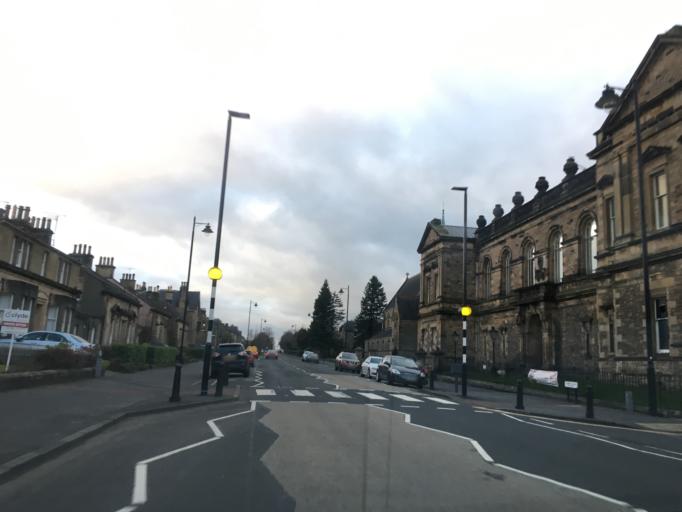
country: GB
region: Scotland
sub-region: Stirling
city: Stirling
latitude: 56.1177
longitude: -3.9413
